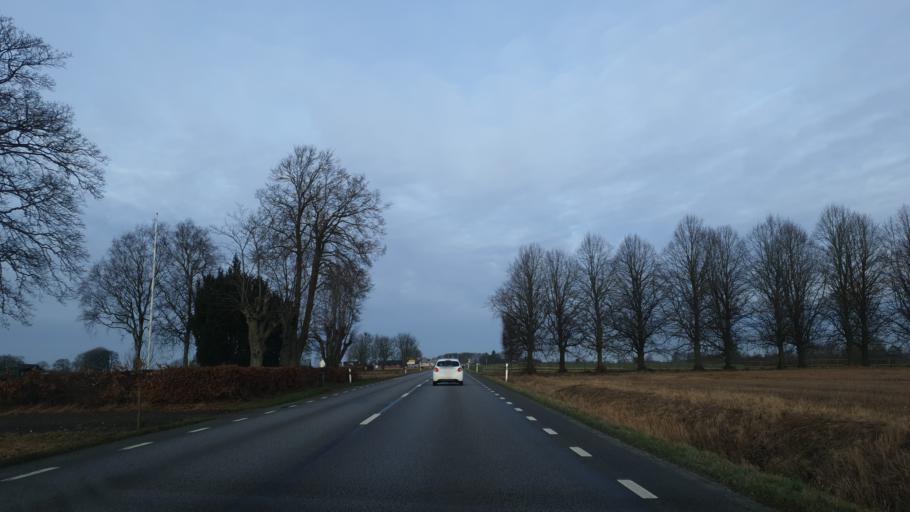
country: SE
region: Skane
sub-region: Horby Kommun
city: Hoerby
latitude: 55.7713
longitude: 13.6740
